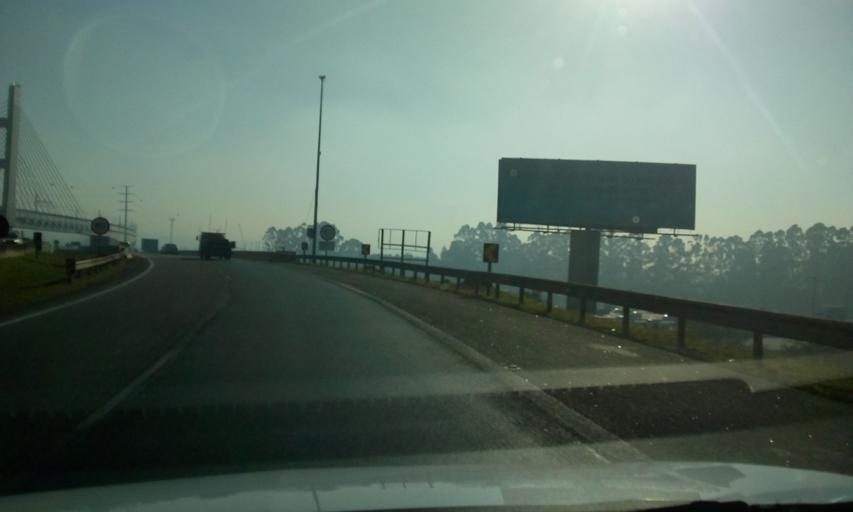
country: BR
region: Sao Paulo
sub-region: Guarulhos
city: Guarulhos
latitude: -23.4744
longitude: -46.4925
